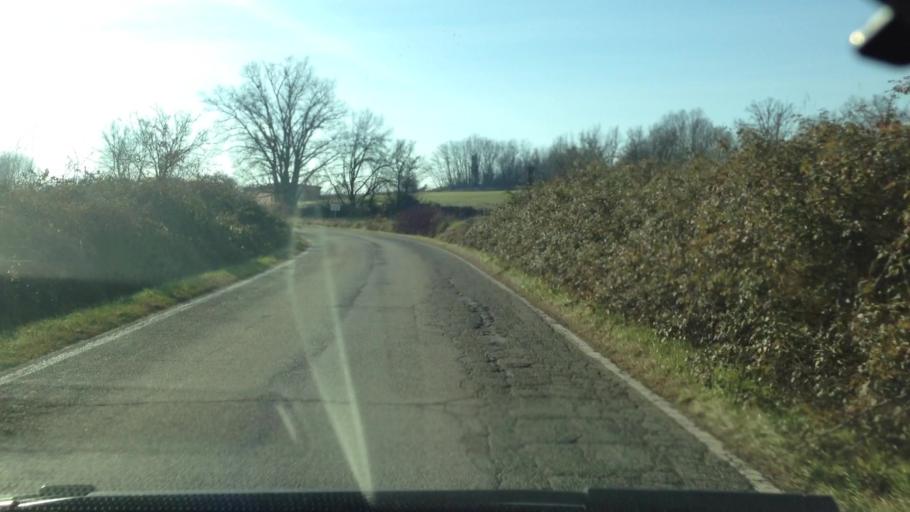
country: IT
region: Piedmont
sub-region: Provincia di Alessandria
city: Quattordio
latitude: 44.8936
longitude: 8.4052
